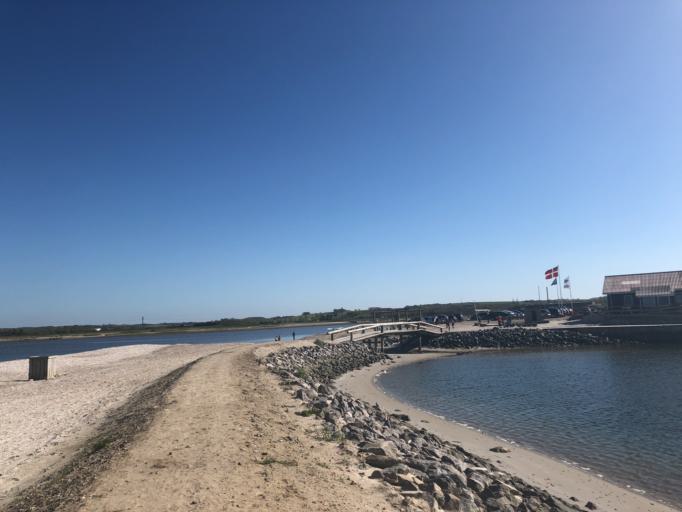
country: DK
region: Central Jutland
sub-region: Holstebro Kommune
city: Vinderup
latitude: 56.4804
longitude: 8.7217
